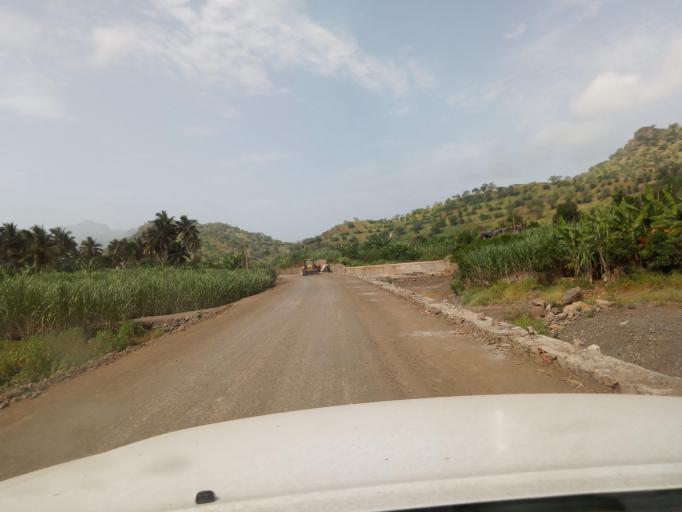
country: CV
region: Santa Cruz
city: Santa Cruz
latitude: 15.1135
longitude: -23.5524
